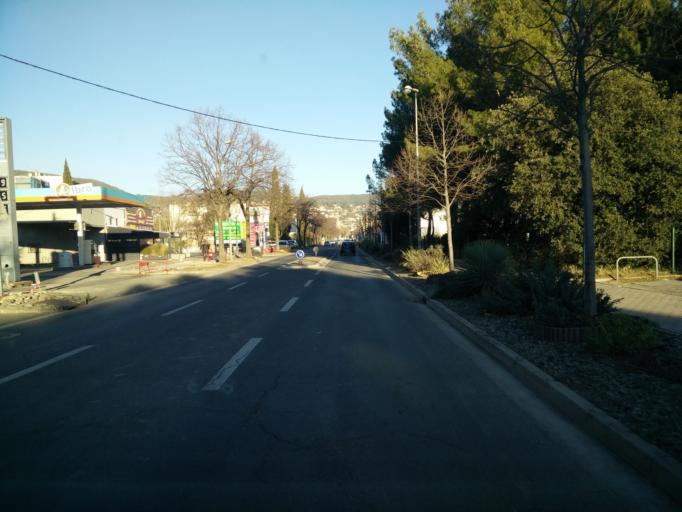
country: FR
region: Provence-Alpes-Cote d'Azur
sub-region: Departement du Var
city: Draguignan
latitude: 43.5324
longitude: 6.4507
